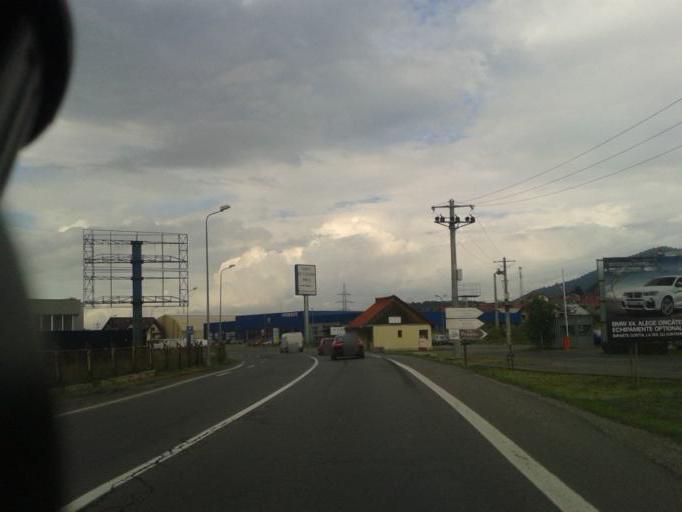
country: RO
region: Brasov
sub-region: Municipiul Sacele
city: Sacele
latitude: 45.6070
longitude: 25.6547
